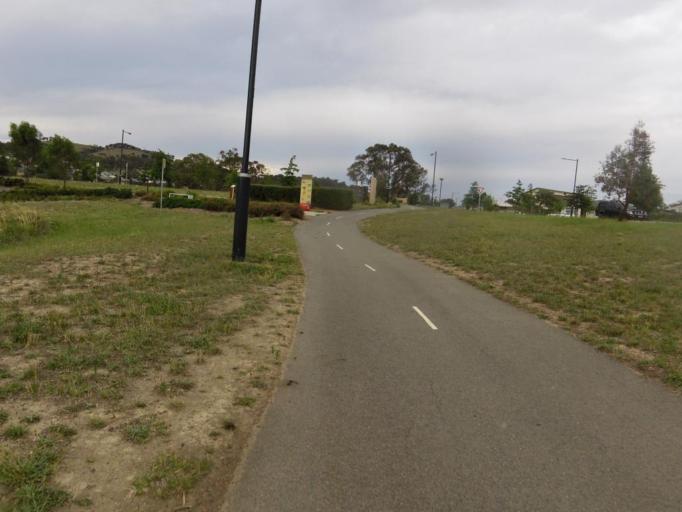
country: AU
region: Australian Capital Territory
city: Kaleen
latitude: -35.1597
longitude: 149.1503
